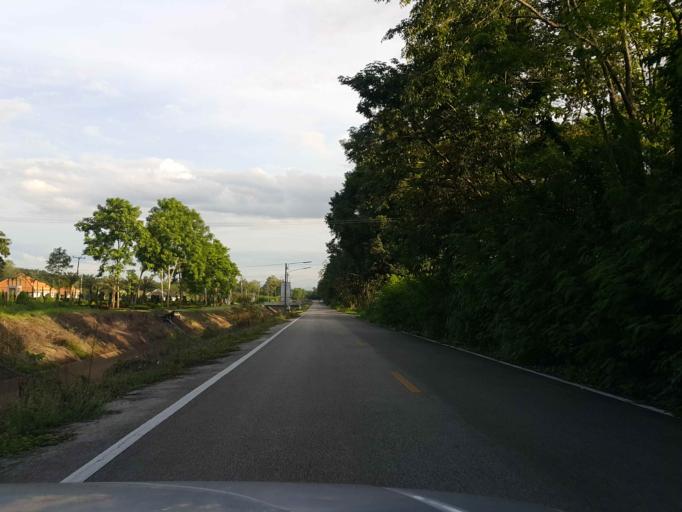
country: TH
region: Chiang Mai
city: San Sai
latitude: 18.9302
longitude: 99.1427
